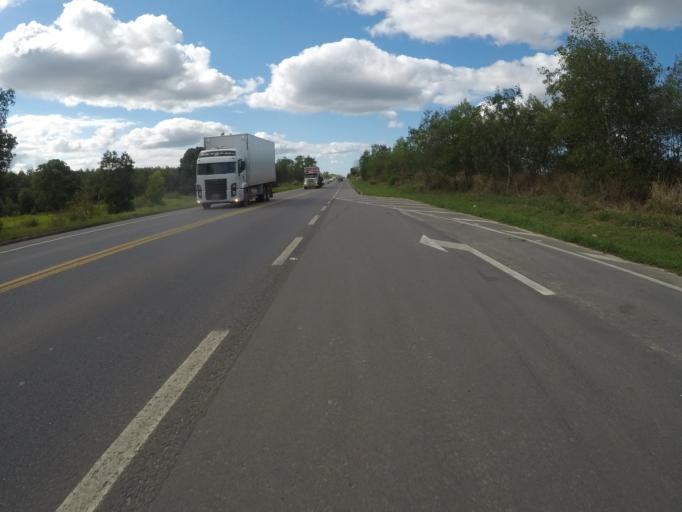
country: BR
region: Espirito Santo
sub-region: Linhares
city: Linhares
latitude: -19.1762
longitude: -40.0909
